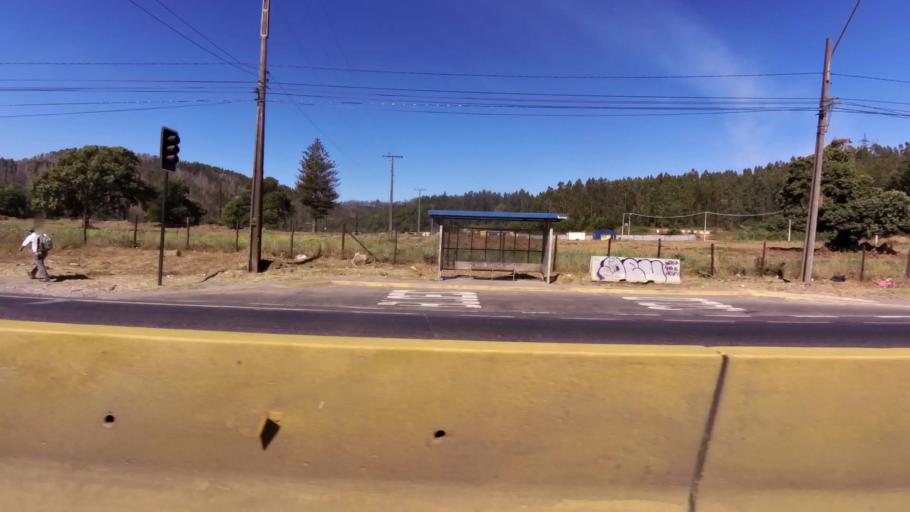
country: CL
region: Biobio
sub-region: Provincia de Concepcion
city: Concepcion
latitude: -36.7980
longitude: -73.0258
